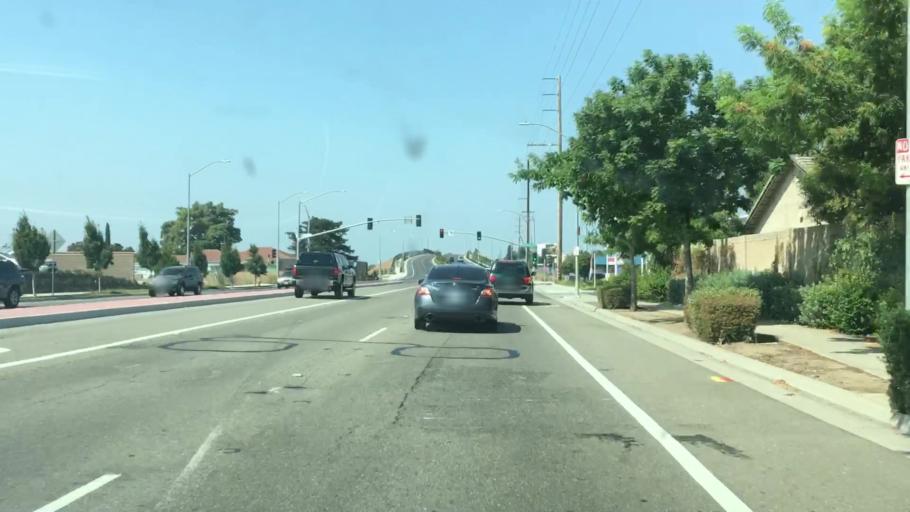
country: US
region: California
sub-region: San Joaquin County
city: Lodi
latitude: 38.1014
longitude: -121.2682
